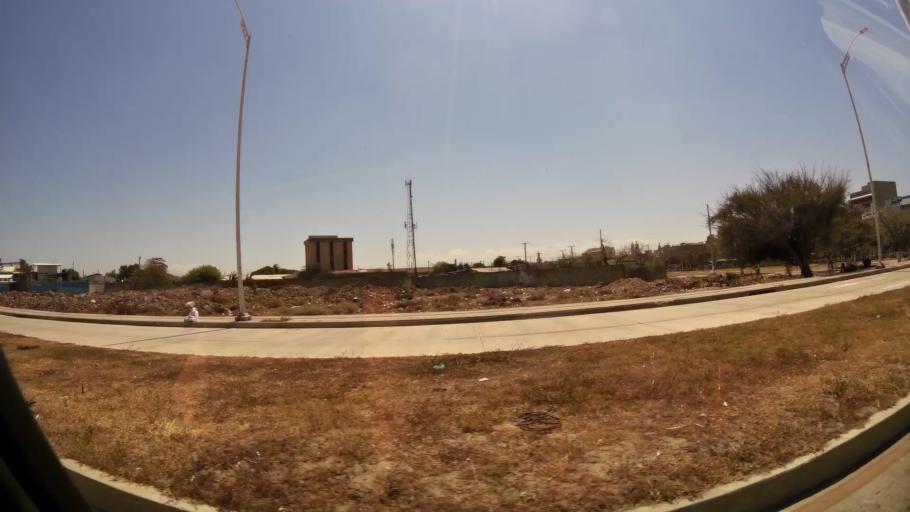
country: CO
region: Atlantico
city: Barranquilla
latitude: 10.9855
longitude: -74.7738
